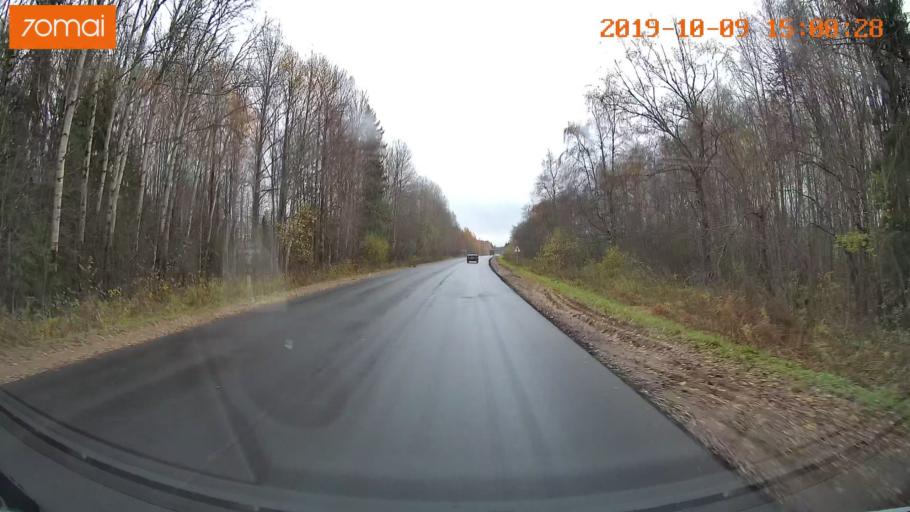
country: RU
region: Kostroma
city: Chistyye Bory
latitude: 58.3089
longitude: 41.6781
